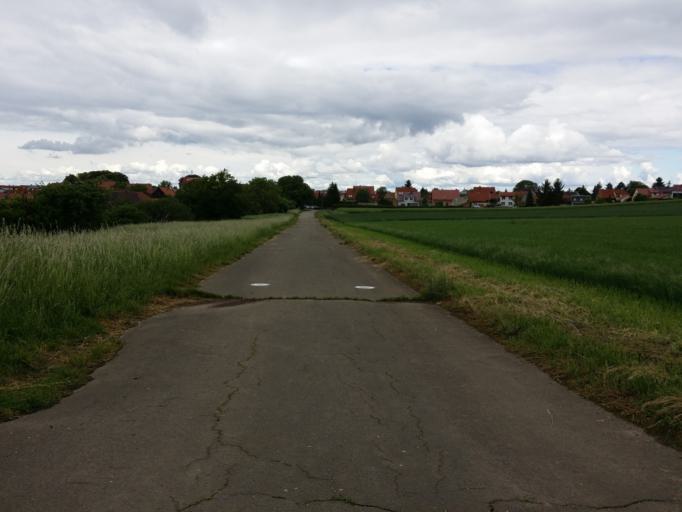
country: DE
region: Thuringia
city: Erfurt
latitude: 50.9614
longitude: 11.0765
